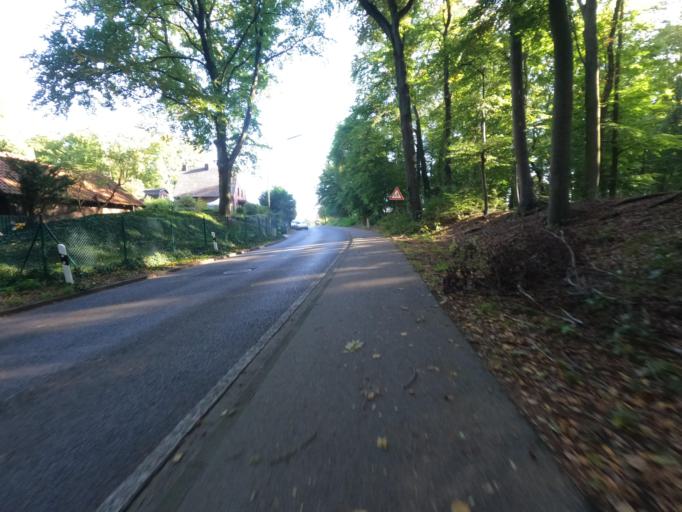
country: DE
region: North Rhine-Westphalia
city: Wegberg
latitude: 51.1711
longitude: 6.2820
